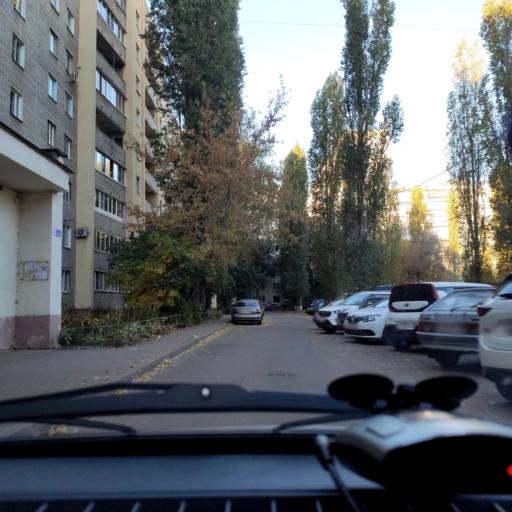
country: RU
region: Voronezj
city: Voronezh
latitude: 51.6854
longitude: 39.1968
